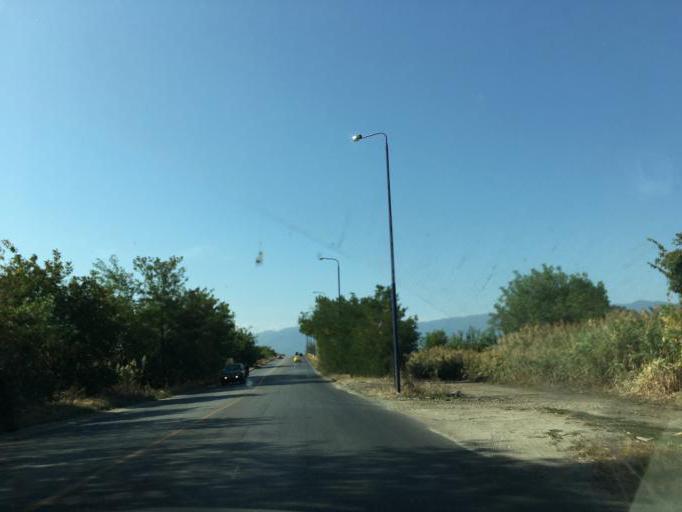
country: BG
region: Pazardzhik
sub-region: Obshtina Pazardzhik
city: Pazardzhik
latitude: 42.1745
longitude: 24.3189
